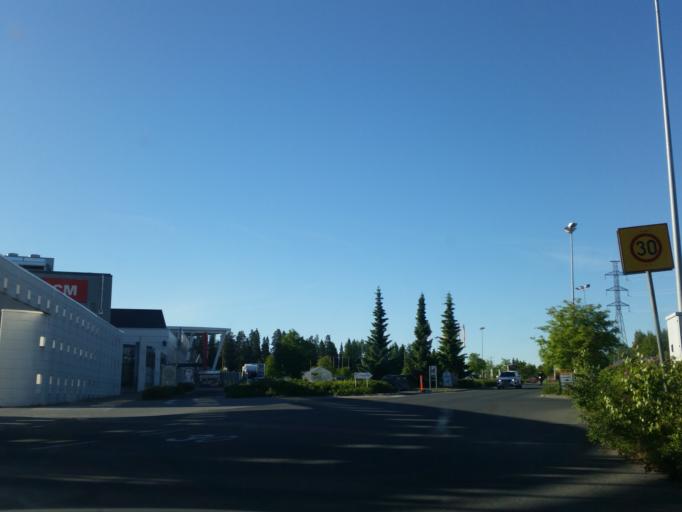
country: FI
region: Northern Savo
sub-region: Kuopio
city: Kuopio
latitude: 62.8627
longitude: 27.6145
